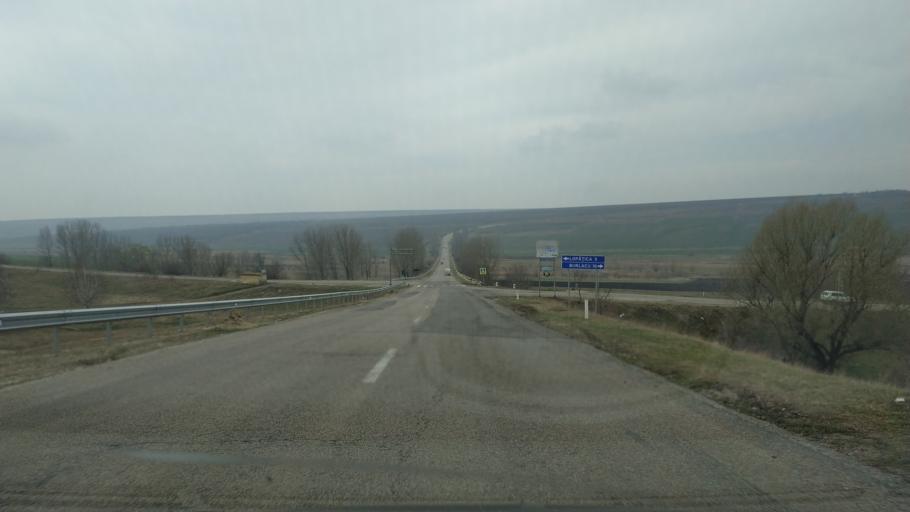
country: MD
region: Cahul
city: Cahul
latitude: 45.9592
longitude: 28.4109
